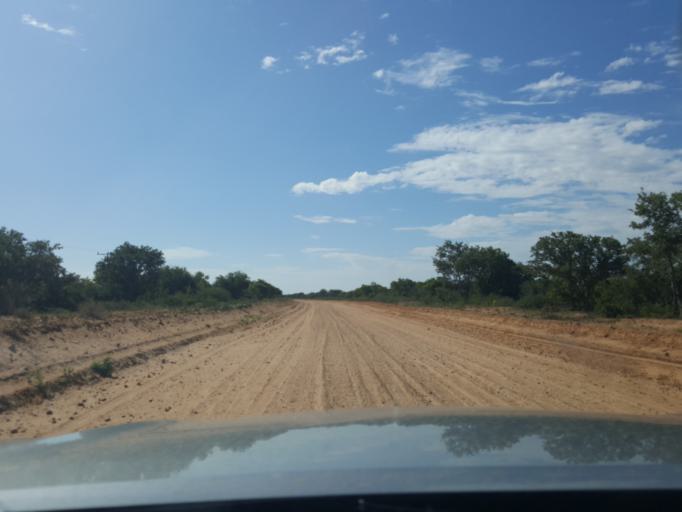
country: BW
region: Kweneng
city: Khudumelapye
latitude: -23.7274
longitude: 24.7419
